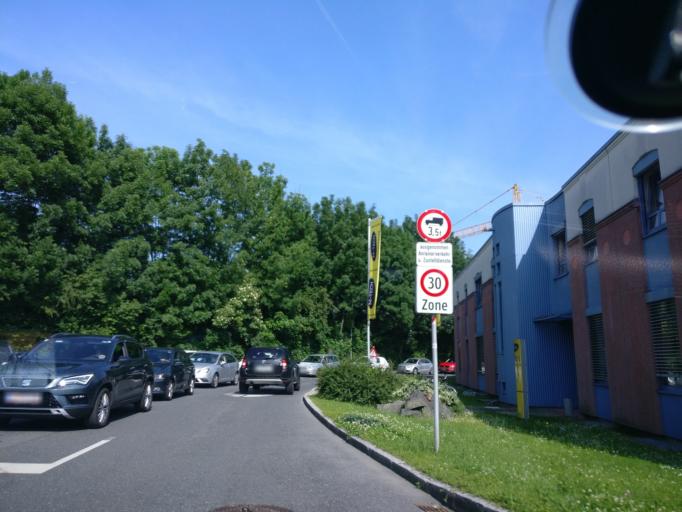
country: AT
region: Carinthia
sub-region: Klagenfurt am Woerthersee
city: Klagenfurt am Woerthersee
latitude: 46.6134
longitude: 14.2926
